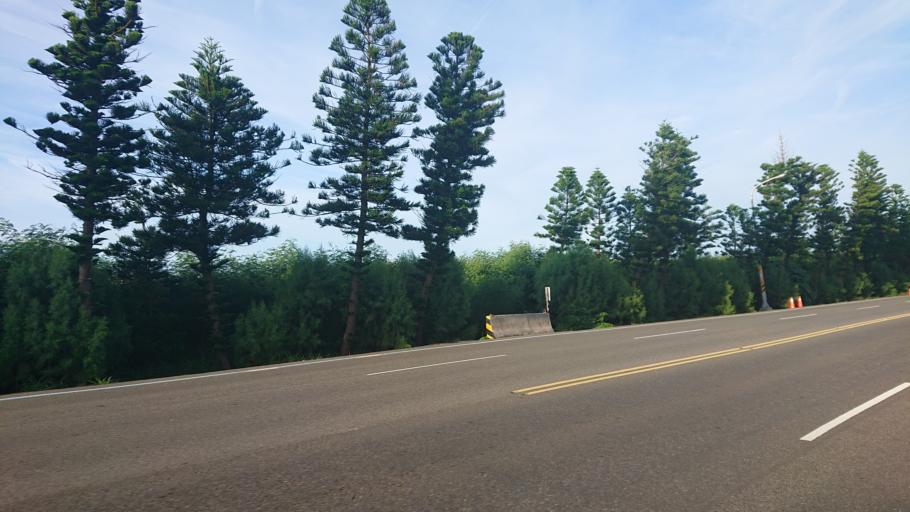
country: TW
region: Taiwan
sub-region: Penghu
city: Ma-kung
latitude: 23.6600
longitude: 119.5620
